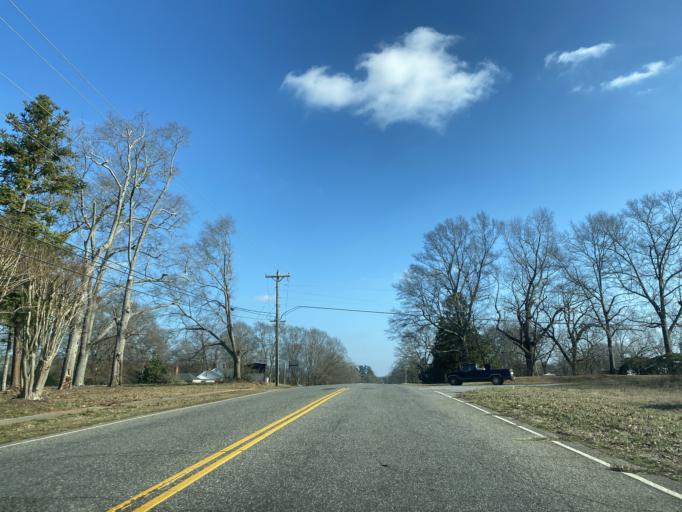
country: US
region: South Carolina
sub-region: Spartanburg County
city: Mayo
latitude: 35.1477
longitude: -81.8521
